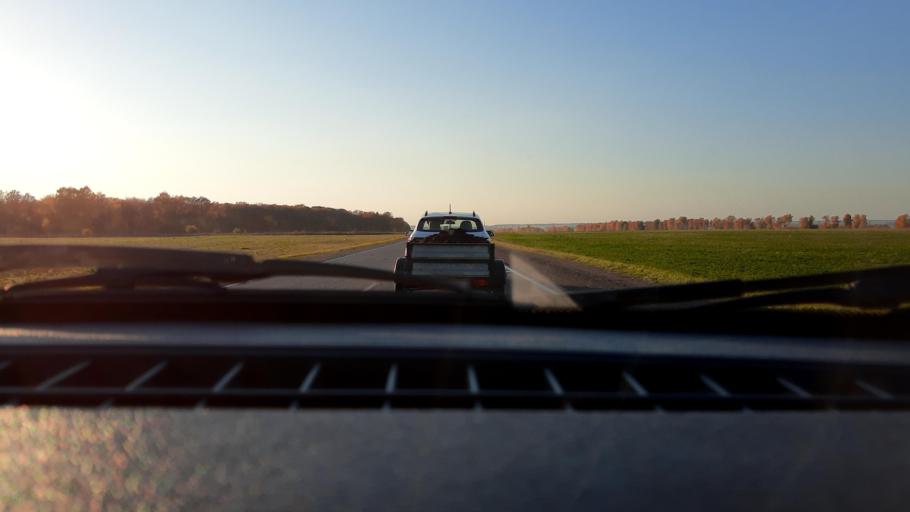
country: RU
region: Bashkortostan
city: Avdon
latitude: 54.8244
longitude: 55.6507
